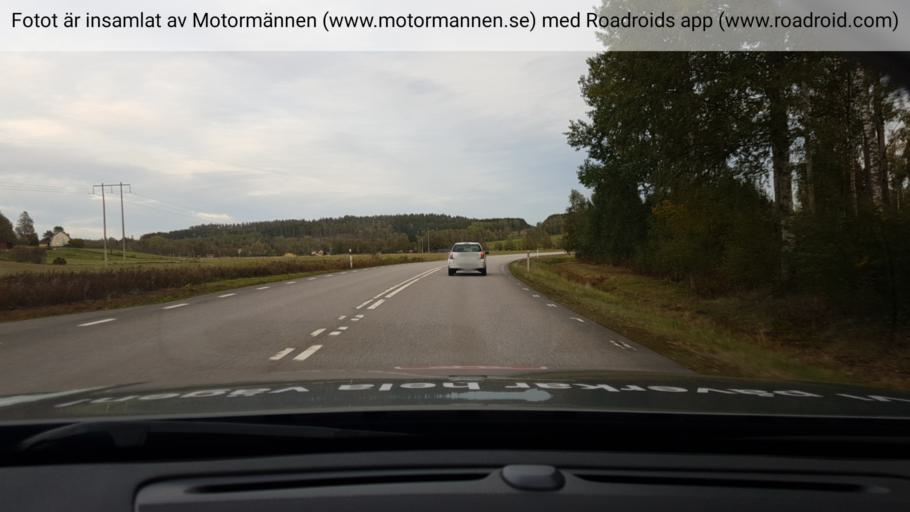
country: SE
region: Vaestra Goetaland
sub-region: Bengtsfors Kommun
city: Billingsfors
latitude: 59.0376
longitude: 12.3222
